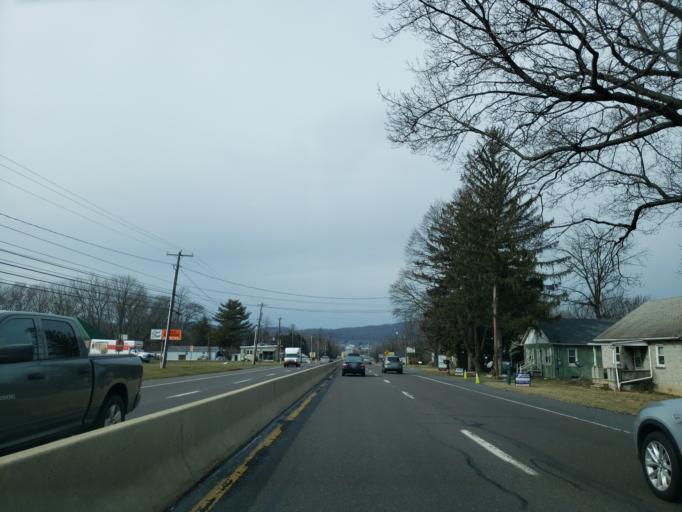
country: US
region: Pennsylvania
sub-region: Lehigh County
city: Coopersburg
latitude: 40.5381
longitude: -75.4111
